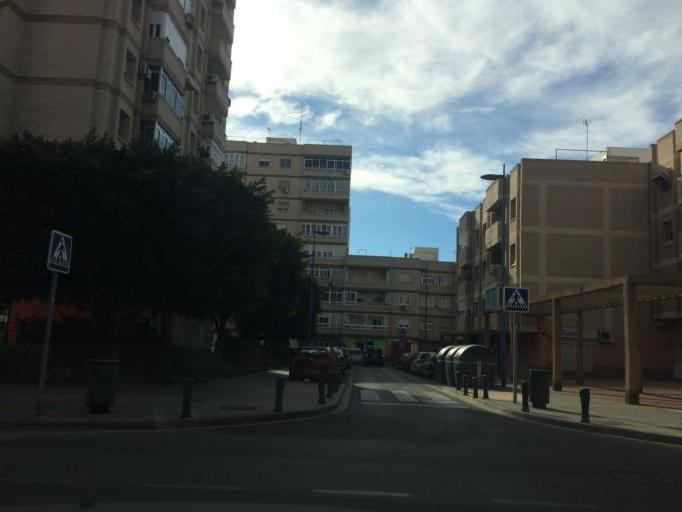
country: ES
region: Andalusia
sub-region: Provincia de Almeria
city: Almeria
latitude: 36.8425
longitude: -2.4493
